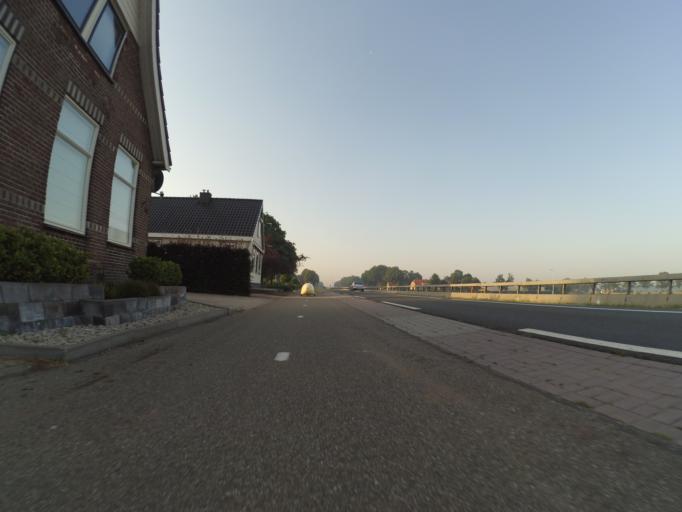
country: NL
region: Overijssel
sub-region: Gemeente Twenterand
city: Vroomshoop
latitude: 52.4333
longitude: 6.5843
